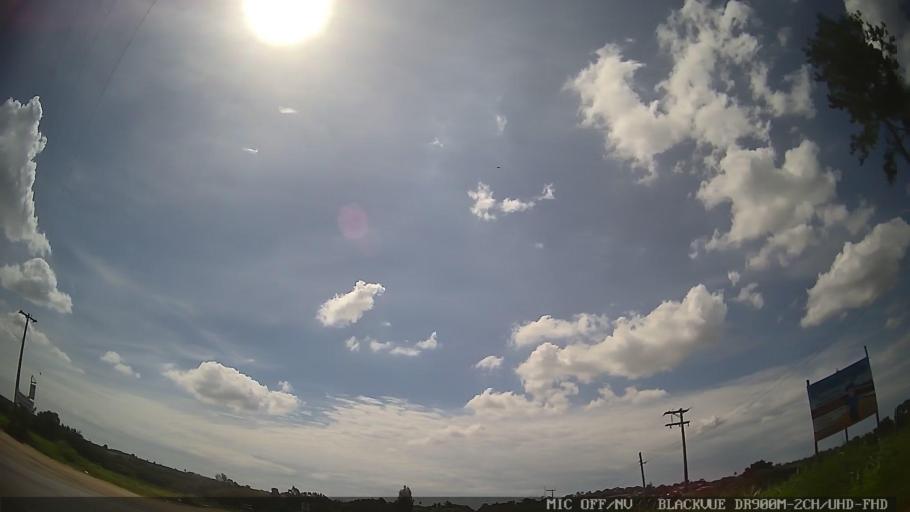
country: BR
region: Sao Paulo
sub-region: Artur Nogueira
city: Artur Nogueira
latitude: -22.6033
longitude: -47.0995
